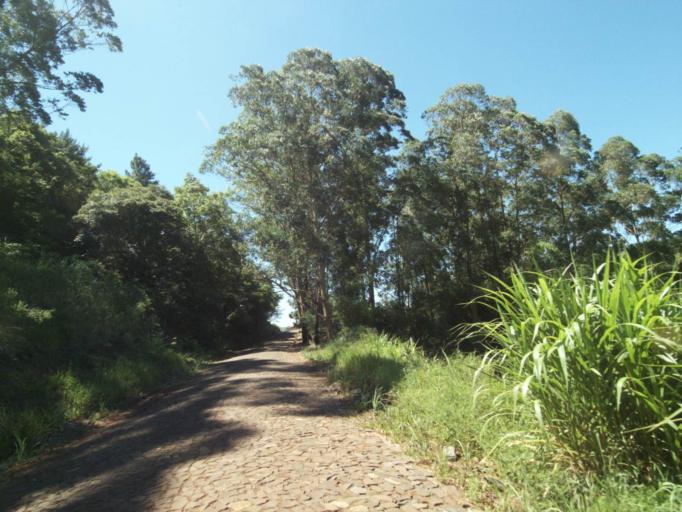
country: BR
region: Parana
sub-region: Ampere
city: Ampere
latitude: -26.1801
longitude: -53.3597
